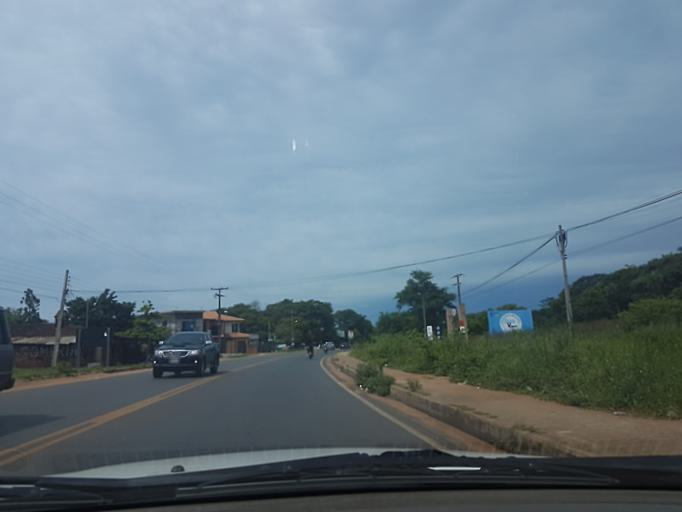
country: PY
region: Central
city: Limpio
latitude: -25.2553
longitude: -57.4739
